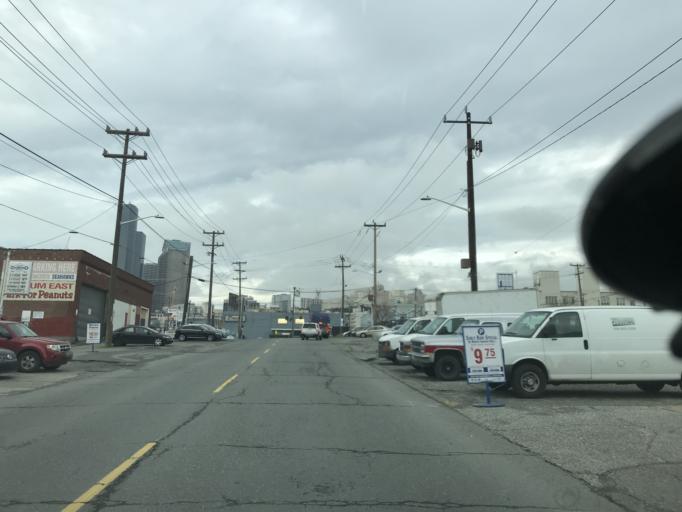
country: US
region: Washington
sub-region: King County
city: Seattle
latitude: 47.5937
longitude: -122.3260
